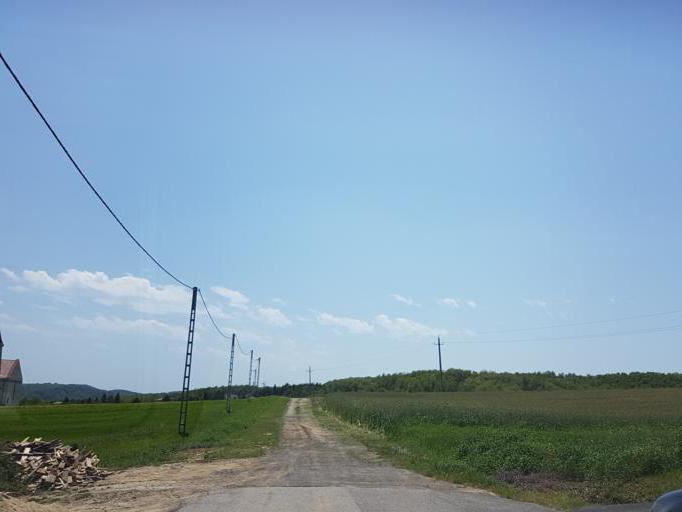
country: HU
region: Zala
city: Zalaegerszeg
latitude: 46.8561
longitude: 16.7761
